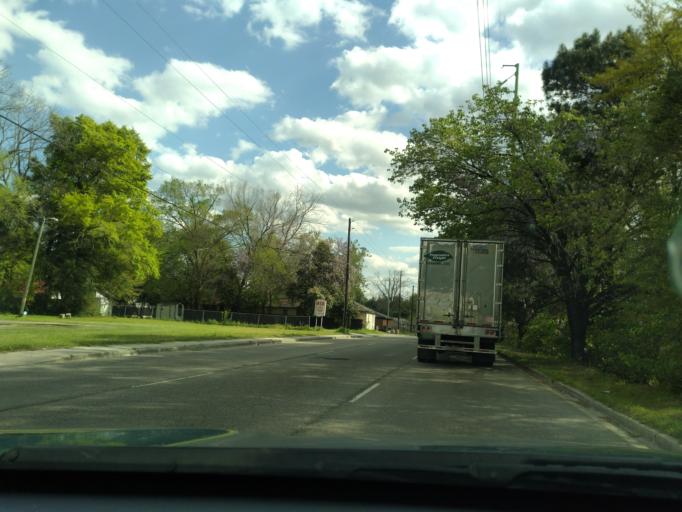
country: US
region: South Carolina
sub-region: Florence County
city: Florence
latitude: 34.1917
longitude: -79.7628
